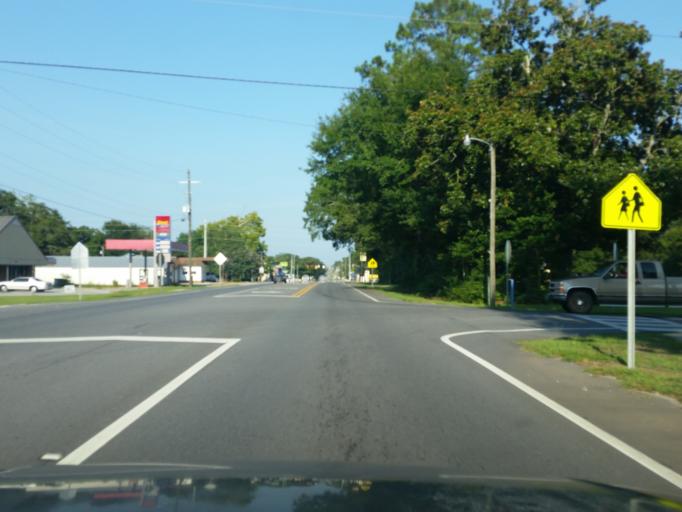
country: US
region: Alabama
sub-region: Baldwin County
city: Elberta
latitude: 30.4143
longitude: -87.6008
